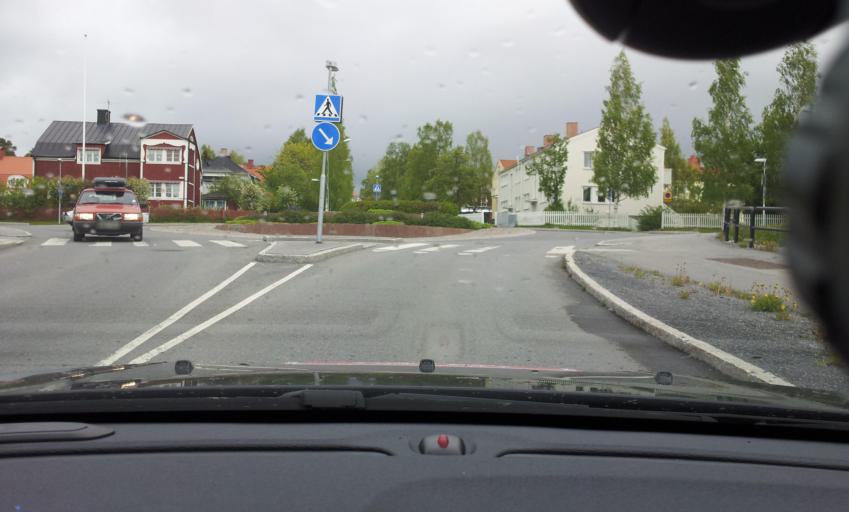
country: SE
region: Jaemtland
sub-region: OEstersunds Kommun
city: Ostersund
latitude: 63.1653
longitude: 14.6518
